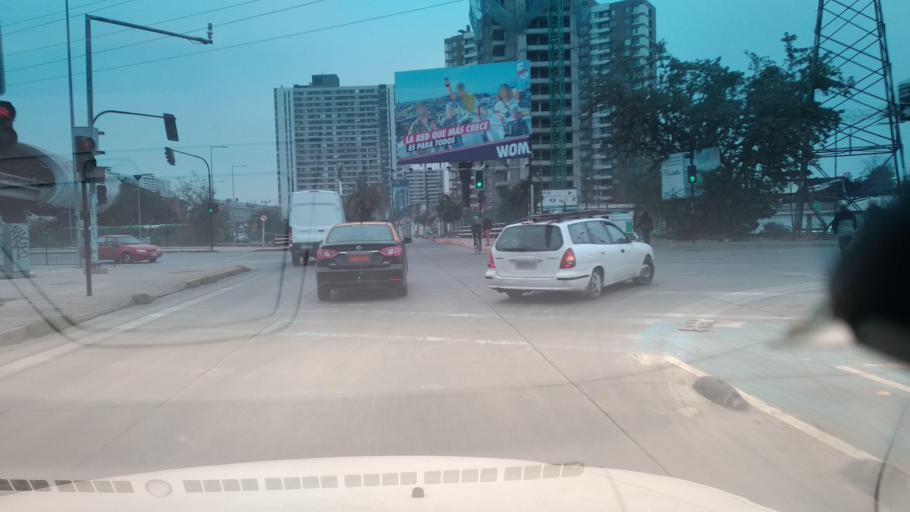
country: CL
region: Santiago Metropolitan
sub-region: Provincia de Santiago
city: Santiago
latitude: -33.4851
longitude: -70.6204
